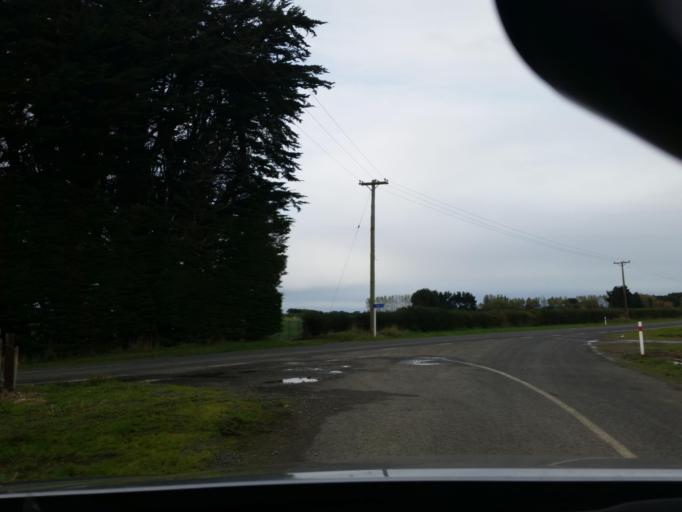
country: NZ
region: Southland
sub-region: Invercargill City
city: Invercargill
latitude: -46.3095
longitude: 168.3034
